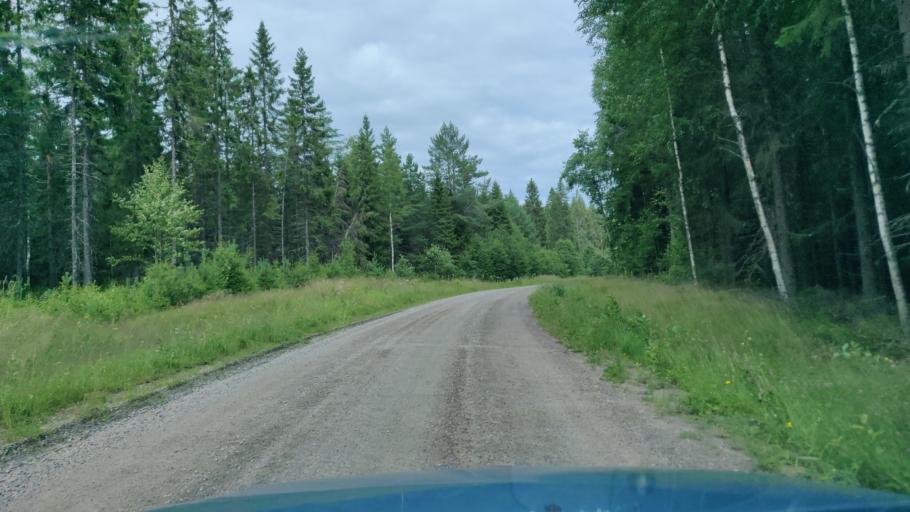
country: SE
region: Vaermland
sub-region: Hagfors Kommun
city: Hagfors
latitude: 59.9405
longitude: 13.5950
